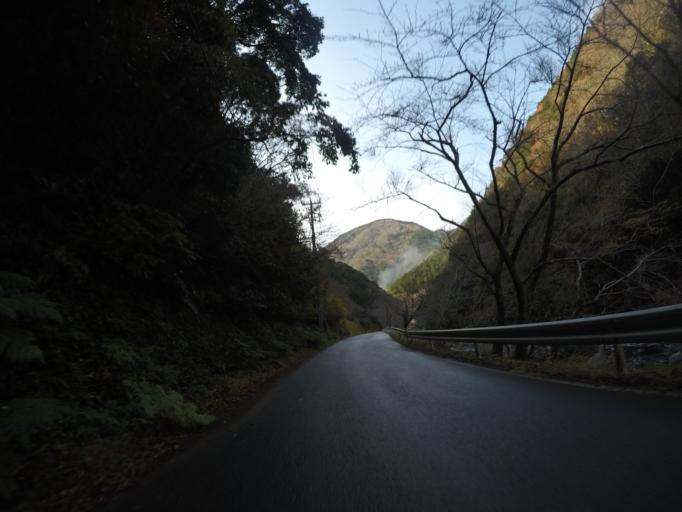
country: JP
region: Shizuoka
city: Heda
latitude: 34.8060
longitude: 138.8149
